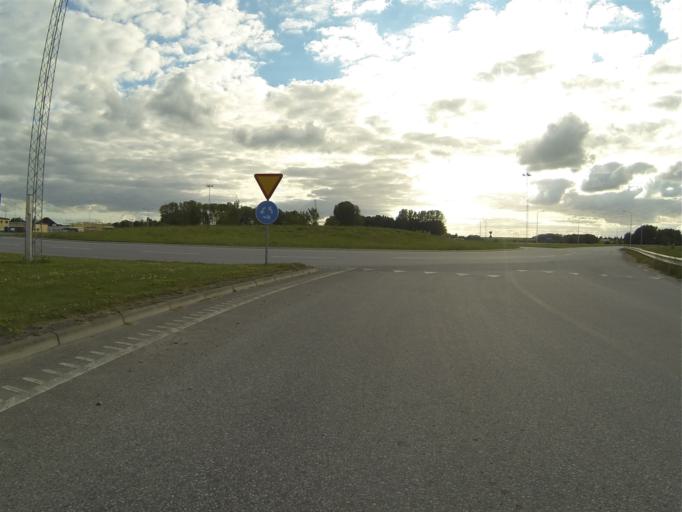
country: SE
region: Skane
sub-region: Staffanstorps Kommun
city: Staffanstorp
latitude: 55.6567
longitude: 13.2209
